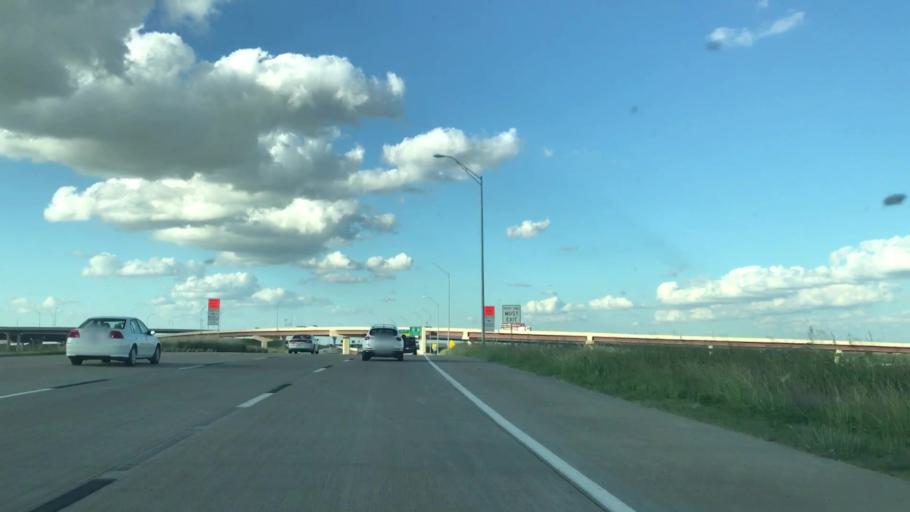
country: US
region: Texas
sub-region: Dallas County
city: Coppell
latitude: 32.9285
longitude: -97.0392
